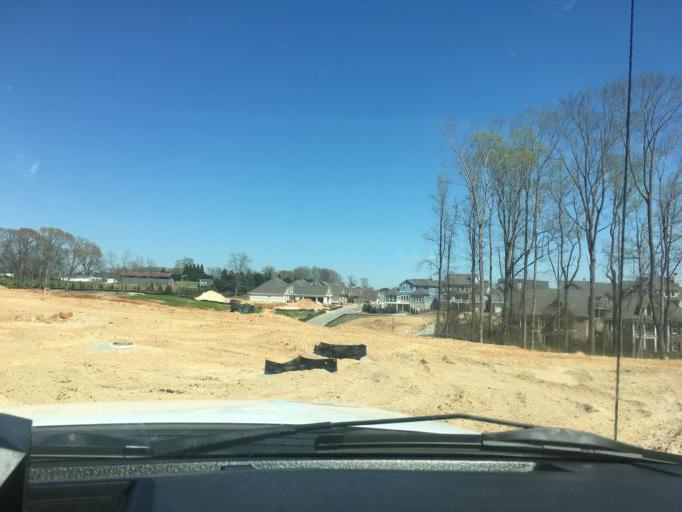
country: US
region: Georgia
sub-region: Jackson County
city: Braselton
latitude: 34.1098
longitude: -83.8439
